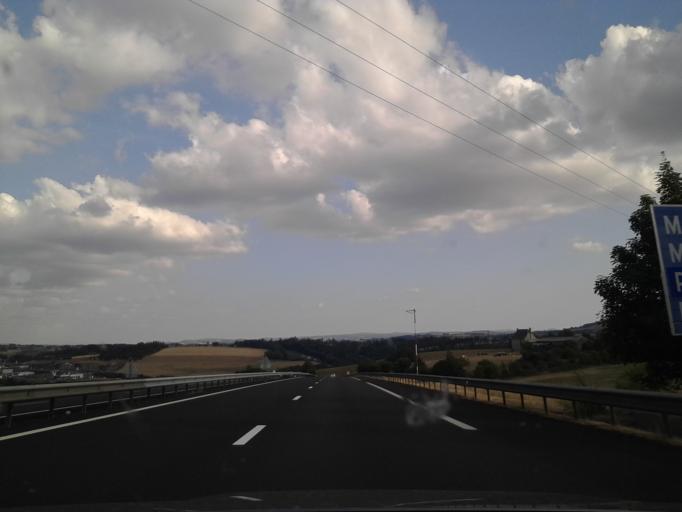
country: FR
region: Auvergne
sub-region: Departement du Cantal
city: Saint-Flour
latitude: 45.0425
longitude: 3.1183
